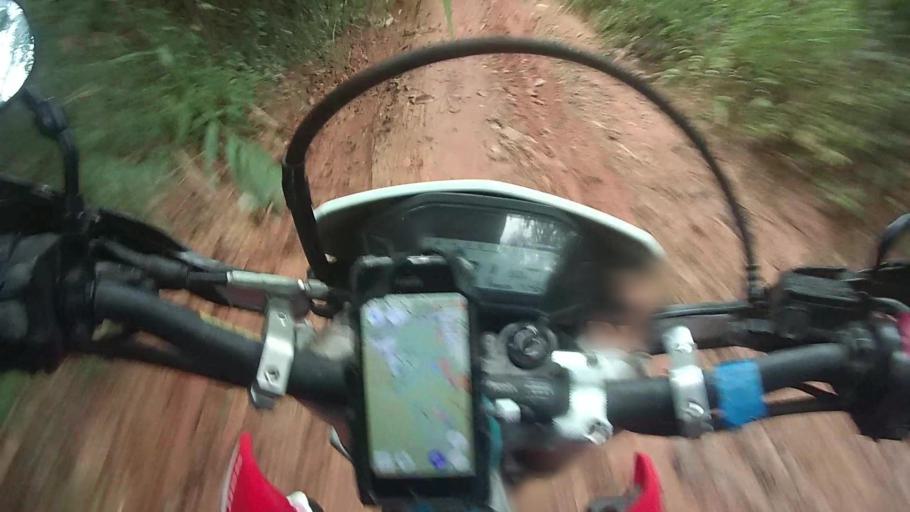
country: TH
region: Chiang Mai
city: Mae On
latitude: 18.8935
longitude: 99.2172
